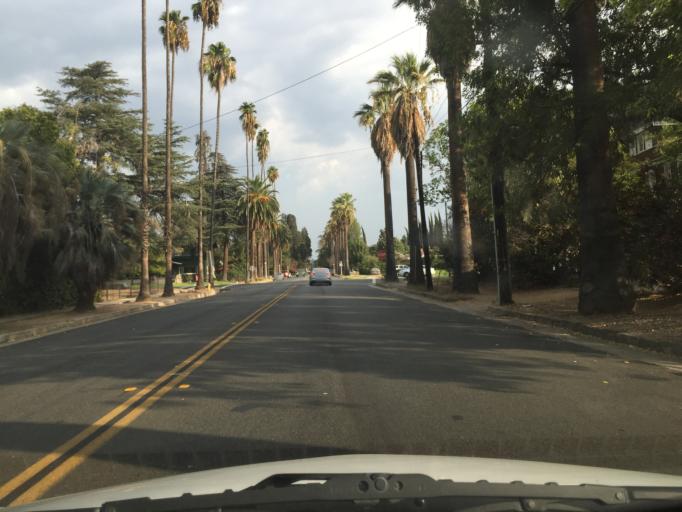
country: US
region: California
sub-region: San Bernardino County
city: Redlands
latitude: 34.0469
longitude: -117.1866
